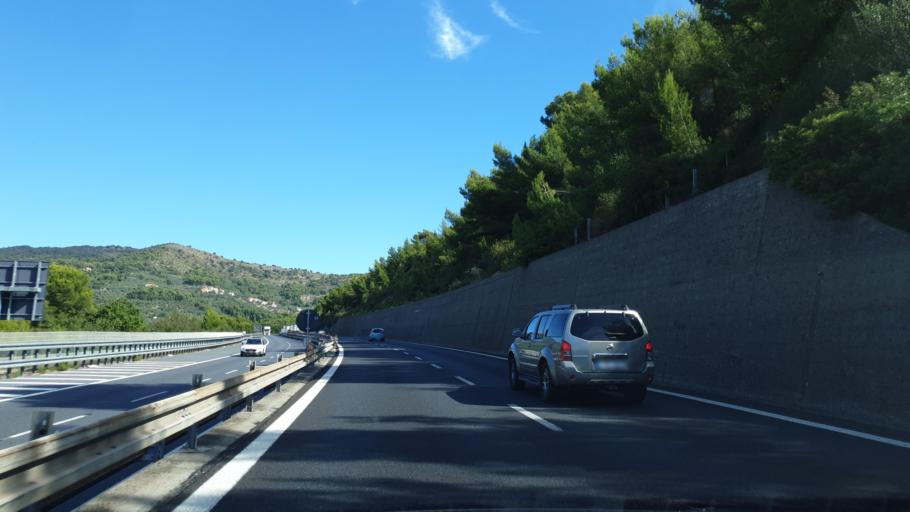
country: IT
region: Liguria
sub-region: Provincia di Imperia
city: San Bartolomeo al Mare
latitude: 43.9363
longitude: 8.1067
